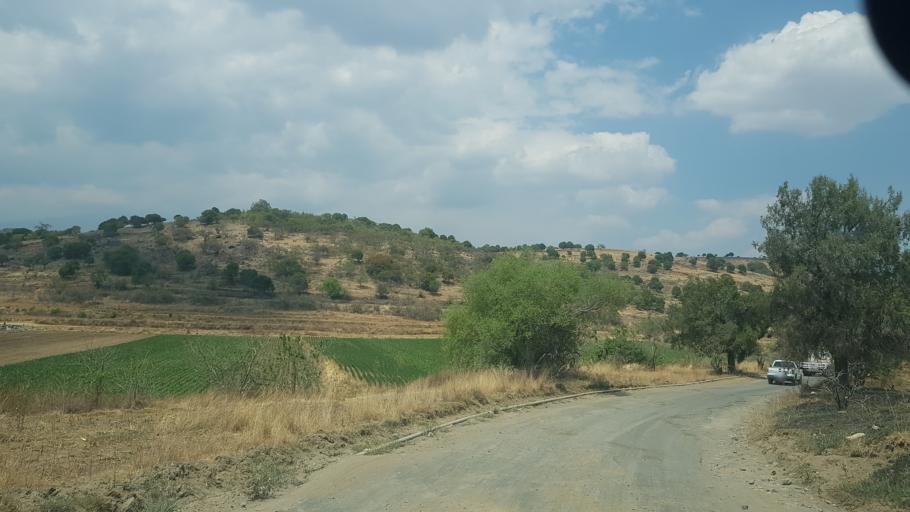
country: MX
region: Puebla
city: San Juan Amecac
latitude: 18.8301
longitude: -98.6219
